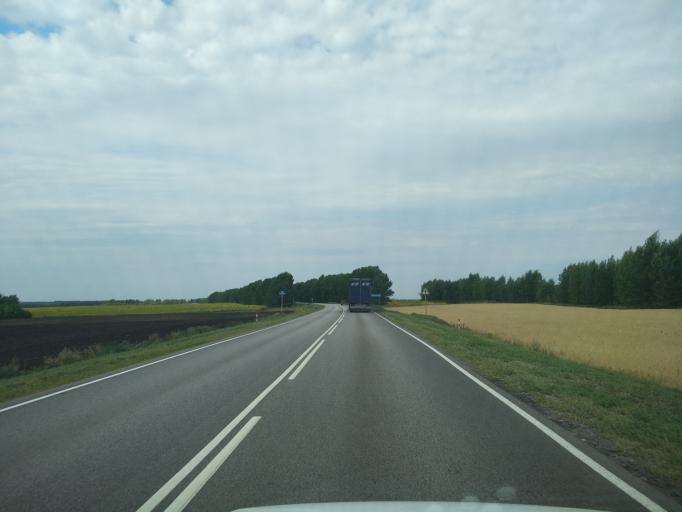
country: RU
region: Voronezj
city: Pereleshinskiy
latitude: 51.8500
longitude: 40.3186
